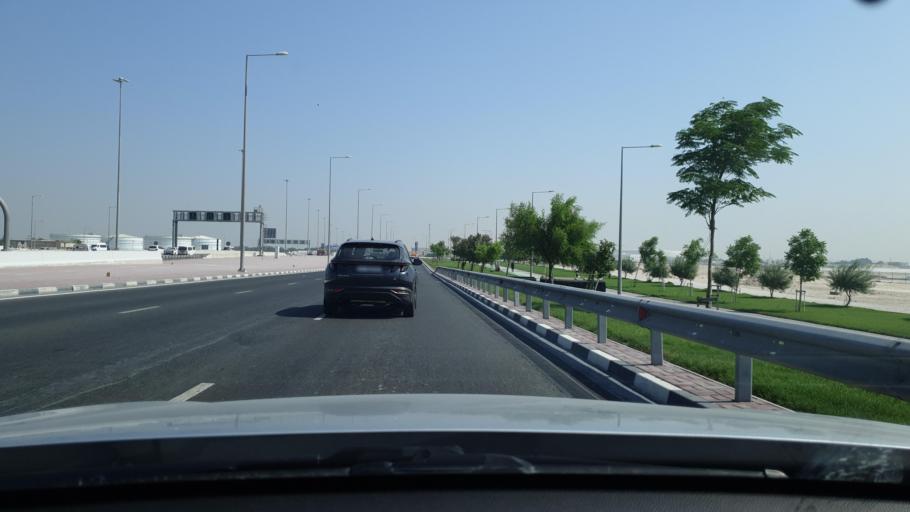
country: QA
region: Baladiyat ad Dawhah
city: Doha
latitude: 25.2273
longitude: 51.5117
